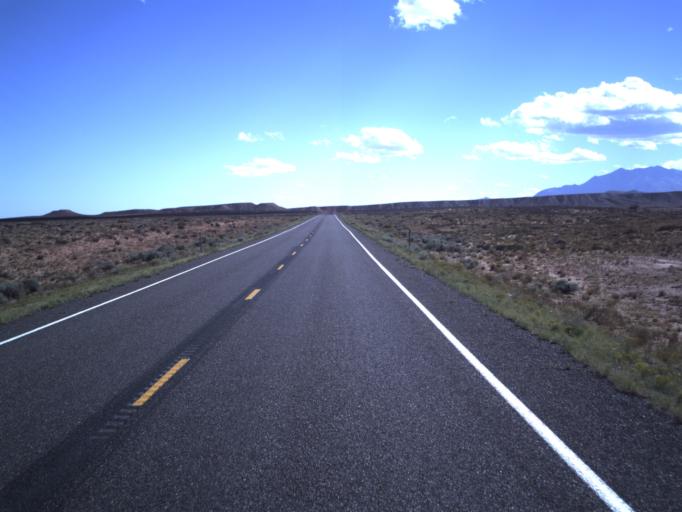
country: US
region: Utah
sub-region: Wayne County
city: Loa
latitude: 38.1759
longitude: -110.6251
